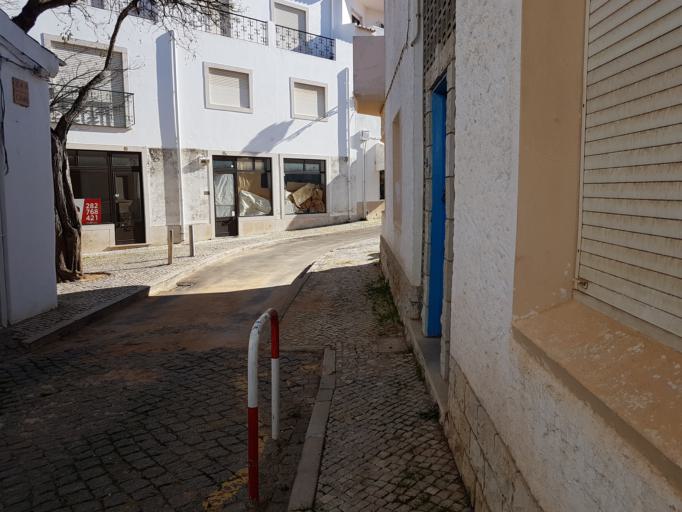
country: PT
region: Faro
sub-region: Lagos
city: Lagos
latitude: 37.1010
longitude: -8.6745
